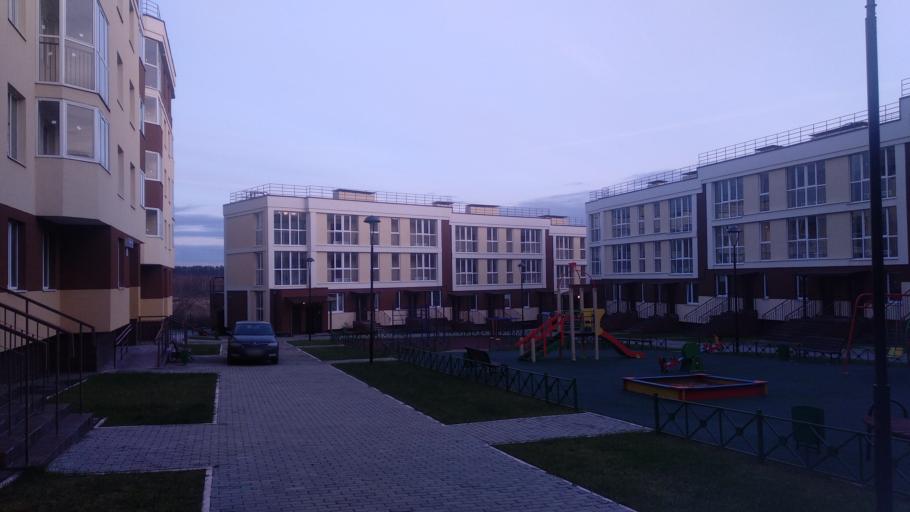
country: RU
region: Moskovskaya
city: Nakhabino
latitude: 55.8560
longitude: 37.1848
